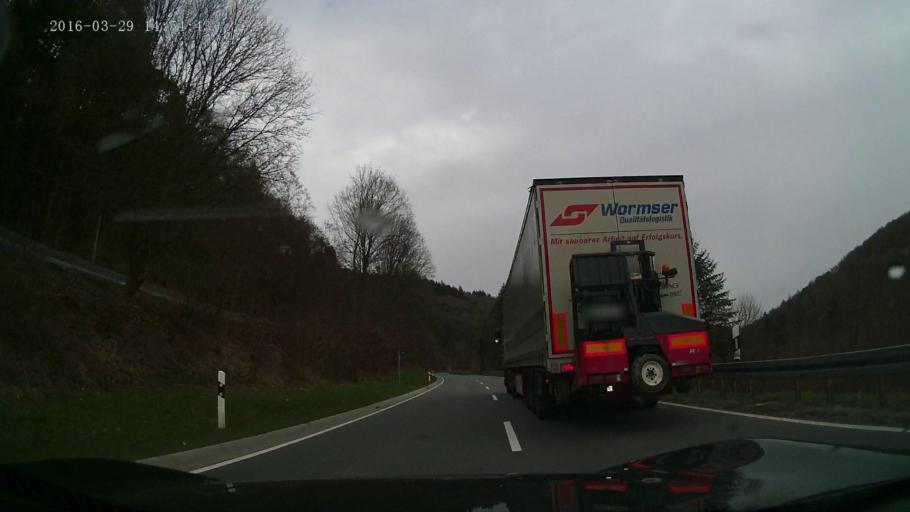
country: DE
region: Baden-Wuerttemberg
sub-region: Karlsruhe Region
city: Walldurn
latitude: 49.6150
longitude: 9.3194
